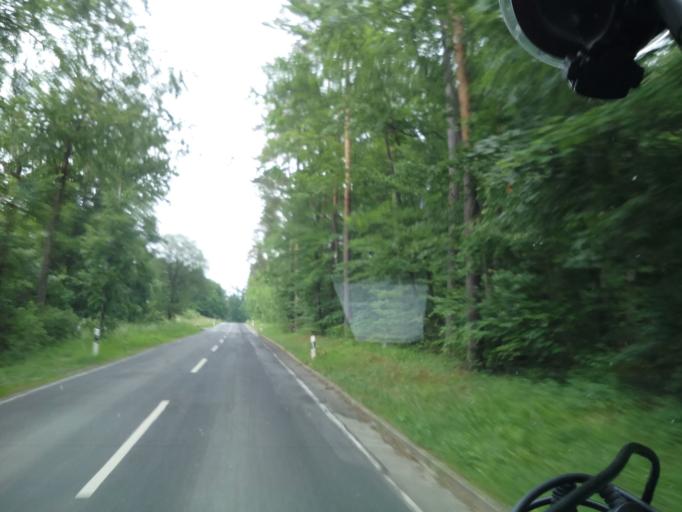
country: DE
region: Bavaria
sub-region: Regierungsbezirk Unterfranken
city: Hendungen
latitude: 50.3957
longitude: 10.3631
